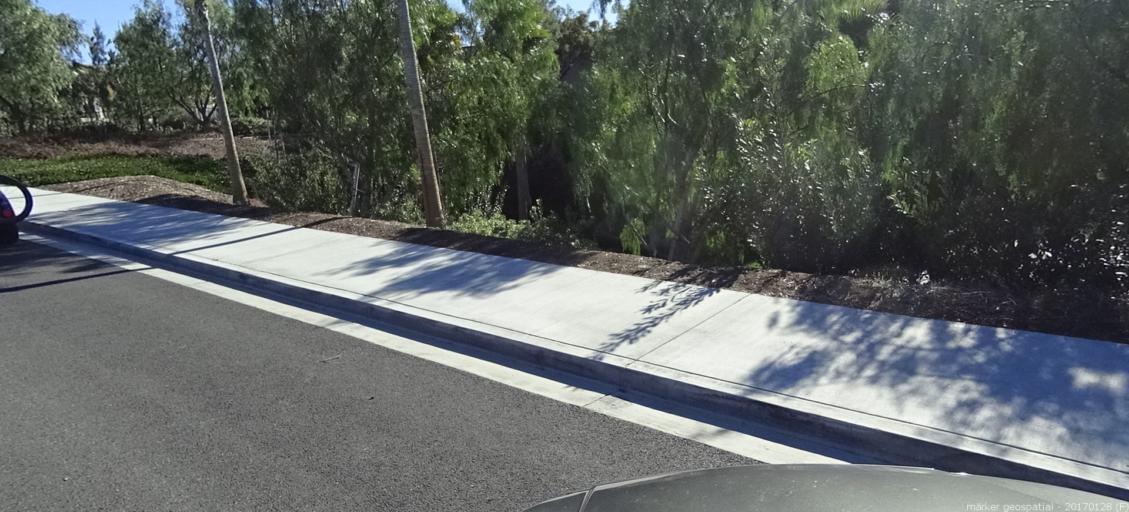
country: US
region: California
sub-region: Orange County
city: Lake Forest
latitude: 33.6699
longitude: -117.6823
